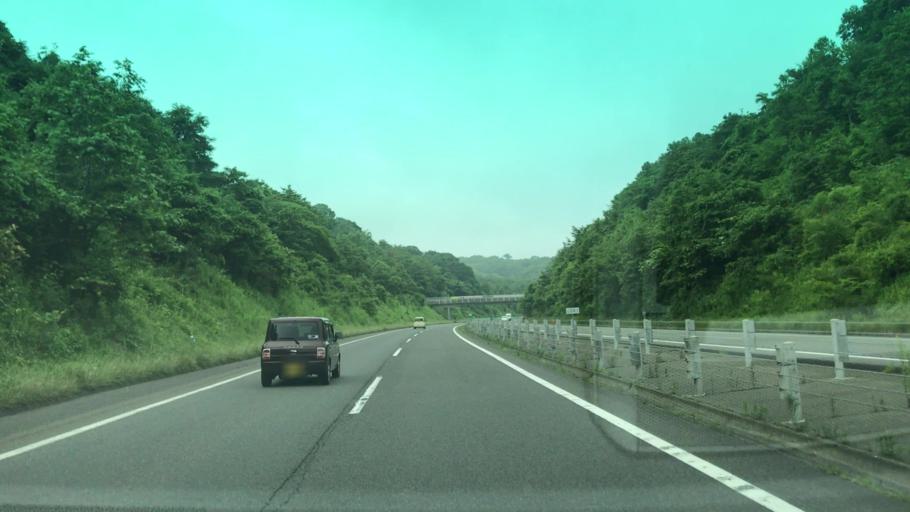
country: JP
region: Hokkaido
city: Shiraoi
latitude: 42.4797
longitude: 141.2203
